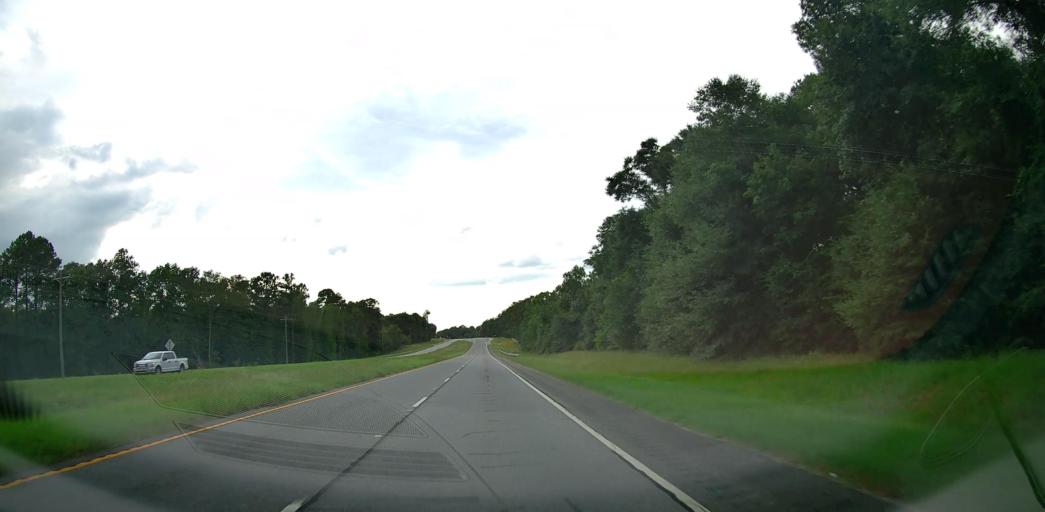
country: US
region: Georgia
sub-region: Pulaski County
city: Hawkinsville
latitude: 32.2753
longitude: -83.4229
